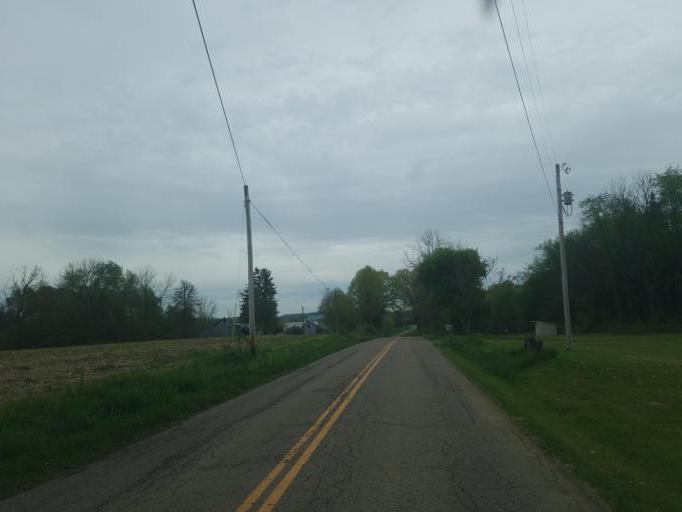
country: US
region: Ohio
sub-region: Knox County
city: Fredericktown
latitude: 40.5414
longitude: -82.5068
